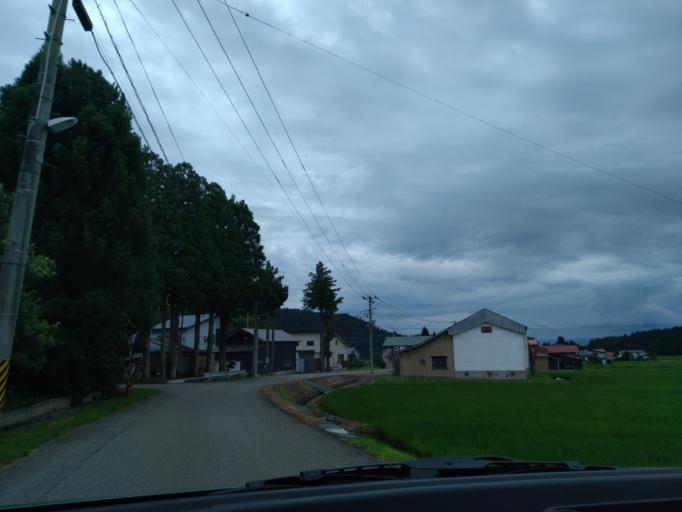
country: JP
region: Akita
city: Yokotemachi
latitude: 39.4245
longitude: 140.6013
